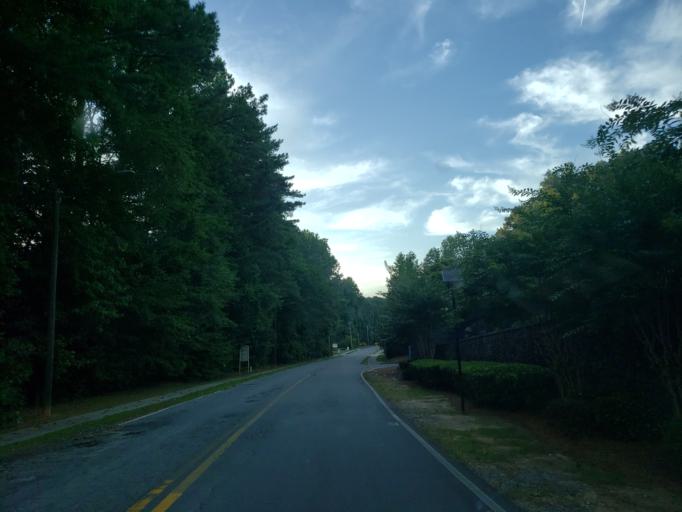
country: US
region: Georgia
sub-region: Cobb County
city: Kennesaw
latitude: 34.0337
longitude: -84.5857
